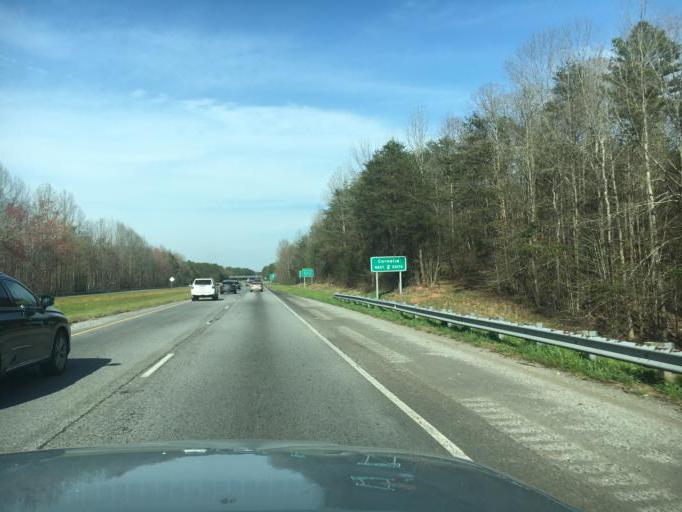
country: US
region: Georgia
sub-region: Habersham County
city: Baldwin
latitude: 34.5097
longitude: -83.5628
